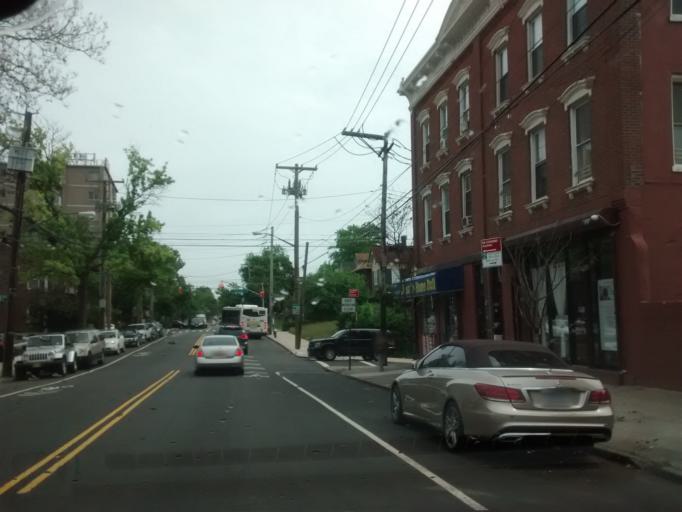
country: US
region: New York
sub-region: Kings County
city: Bensonhurst
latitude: 40.6125
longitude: -74.0650
